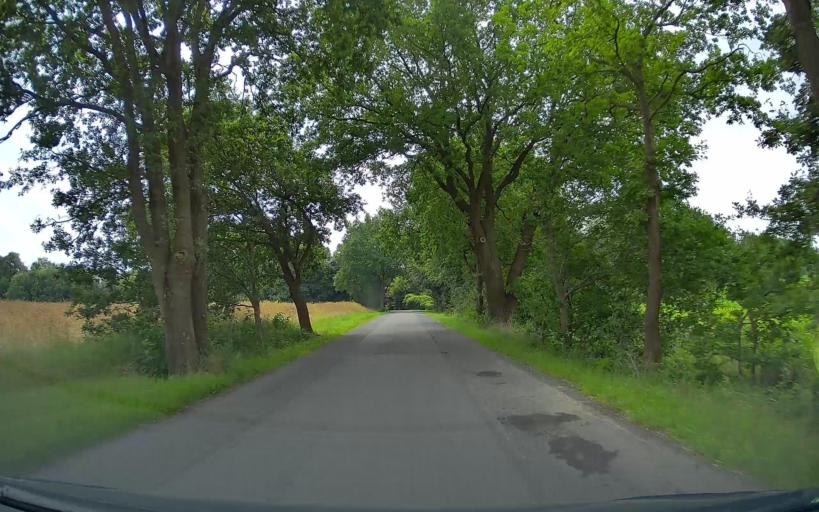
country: DE
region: Lower Saxony
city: Friesoythe
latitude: 53.0067
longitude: 7.8597
